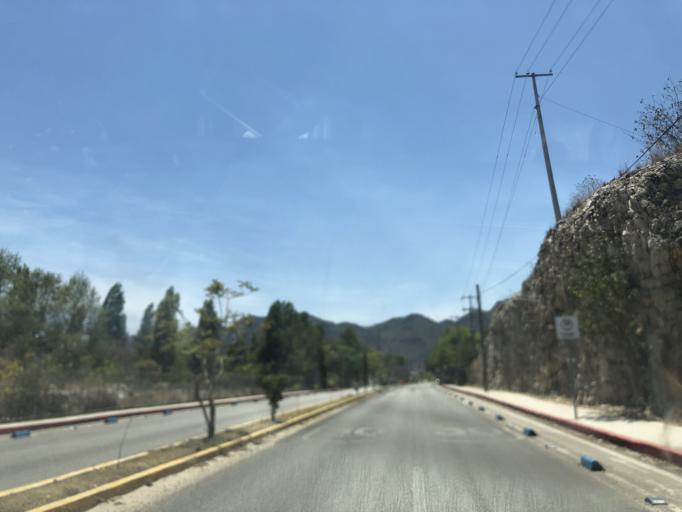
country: MX
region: Chiapas
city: San Cristobal de las Casas
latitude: 16.7310
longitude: -92.6510
